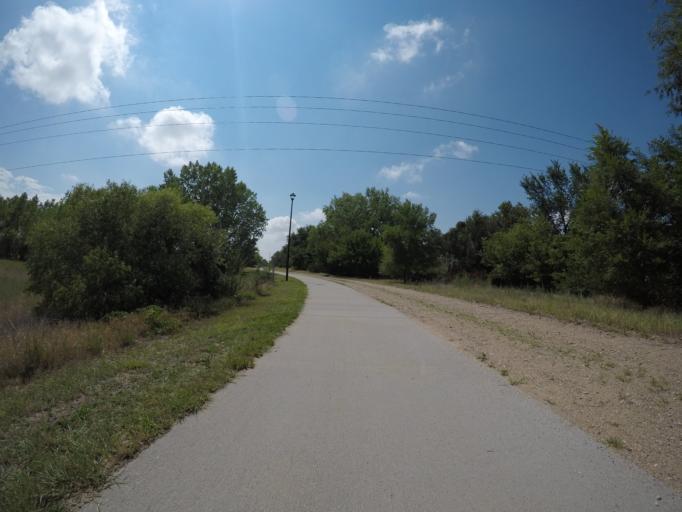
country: US
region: Nebraska
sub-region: Buffalo County
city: Kearney
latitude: 40.6730
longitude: -99.0463
